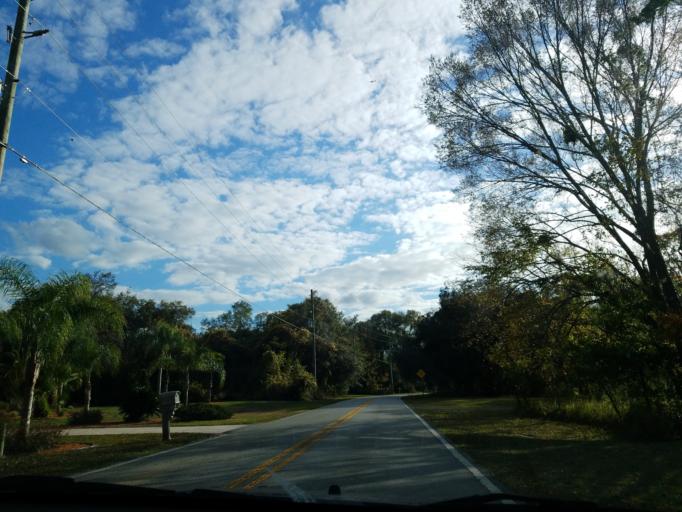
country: US
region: Florida
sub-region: Pasco County
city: Jasmine Estates
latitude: 28.2737
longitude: -82.6504
